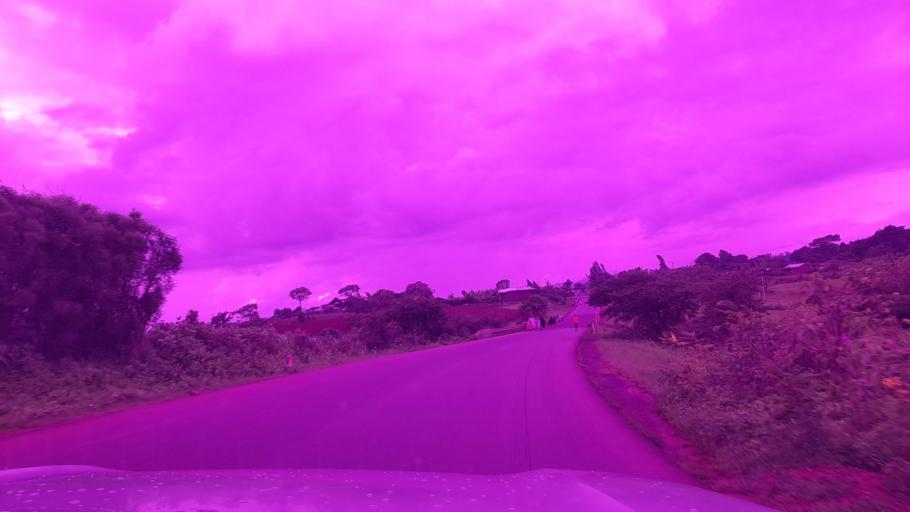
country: ET
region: Oromiya
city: Jima
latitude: 7.7564
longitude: 37.3317
